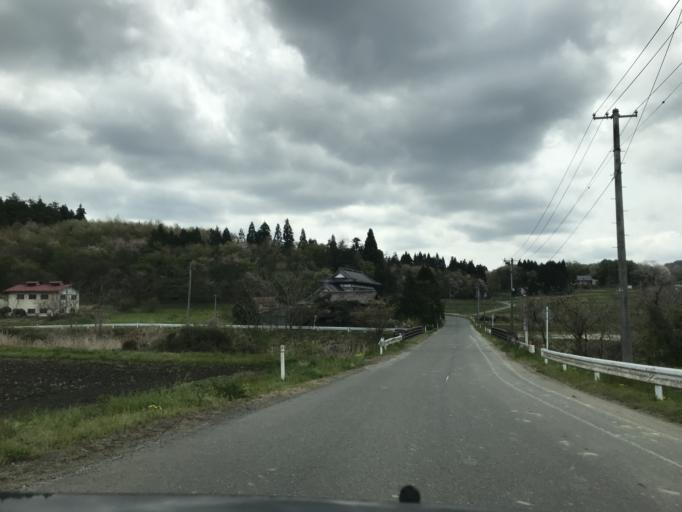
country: JP
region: Iwate
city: Ichinoseki
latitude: 38.8427
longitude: 141.3508
